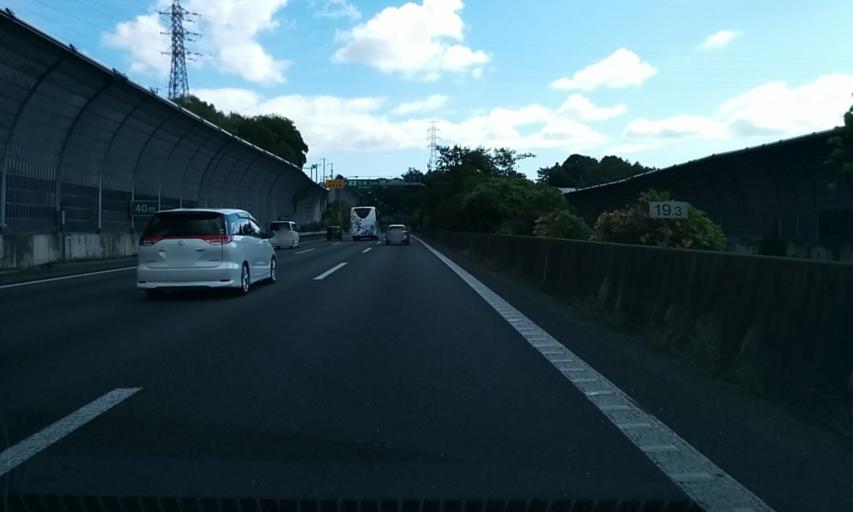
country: JP
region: Hyogo
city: Takarazuka
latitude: 34.8182
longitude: 135.3457
